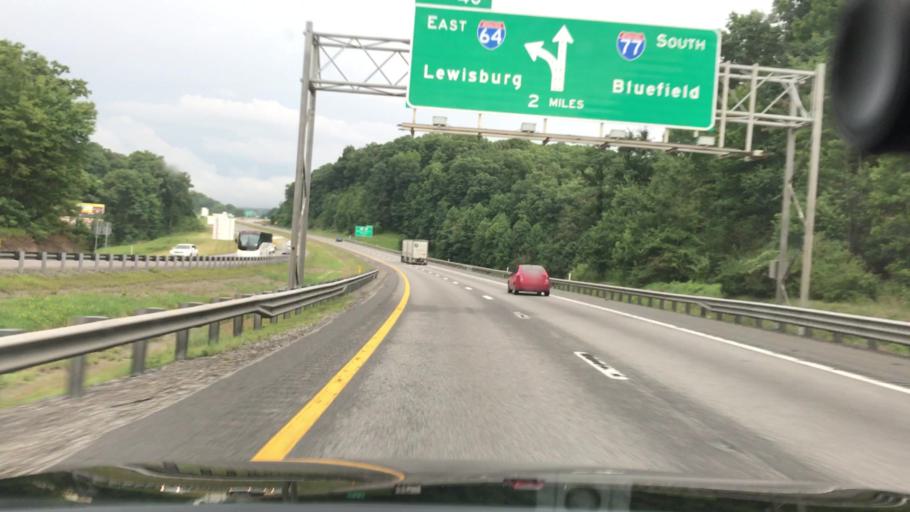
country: US
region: West Virginia
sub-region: Raleigh County
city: Mabscott
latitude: 37.7685
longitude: -81.2190
